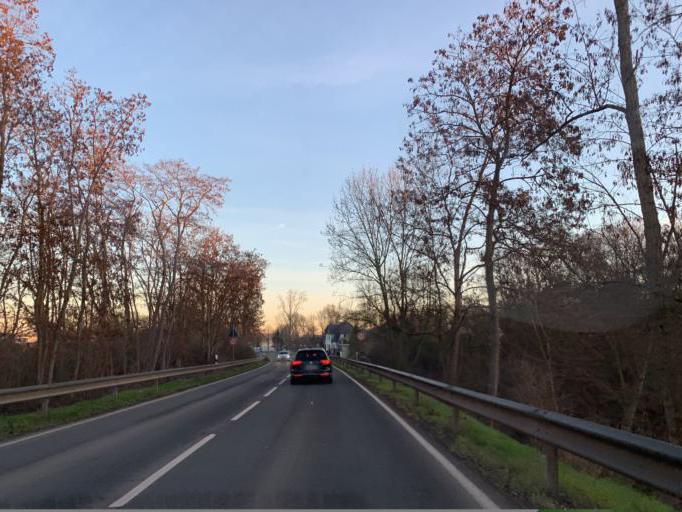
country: DE
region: North Rhine-Westphalia
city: Julich
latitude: 50.9058
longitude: 6.3792
